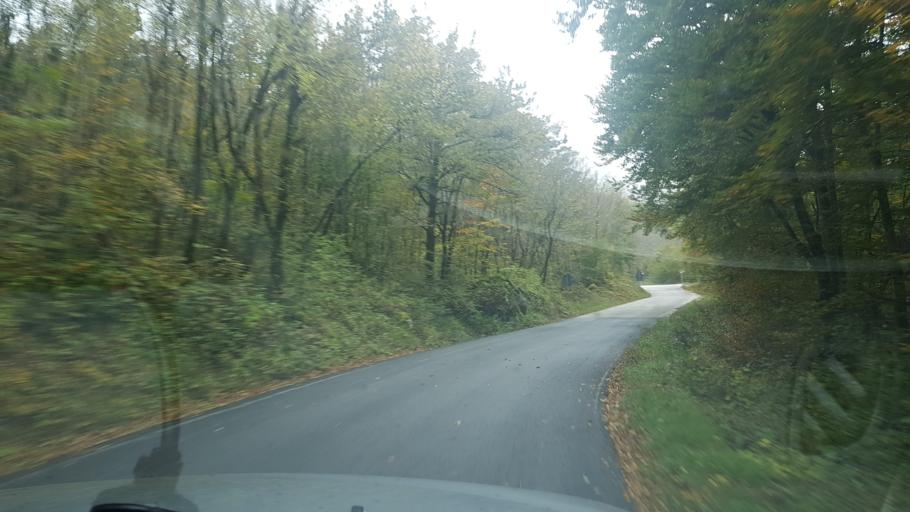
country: HR
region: Istarska
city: Buzet
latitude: 45.4577
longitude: 14.0398
